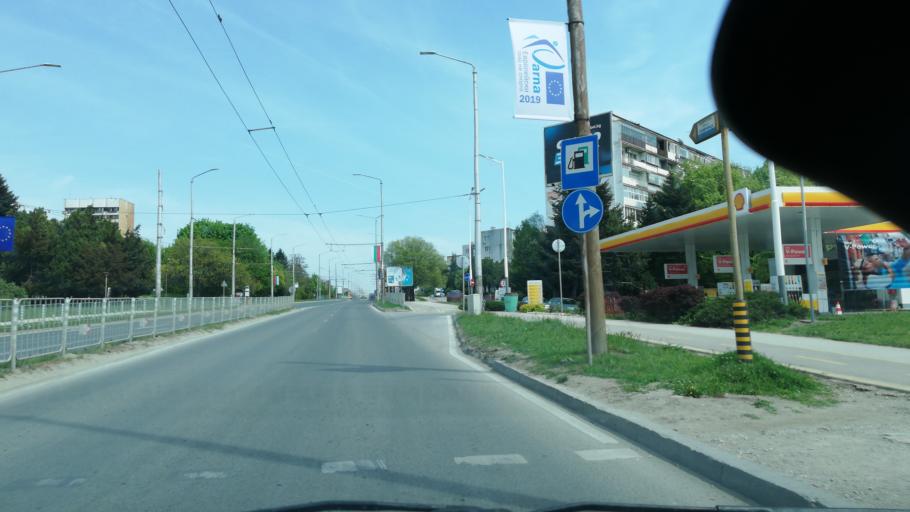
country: BG
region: Varna
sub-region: Obshtina Varna
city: Varna
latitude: 43.2279
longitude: 27.8781
